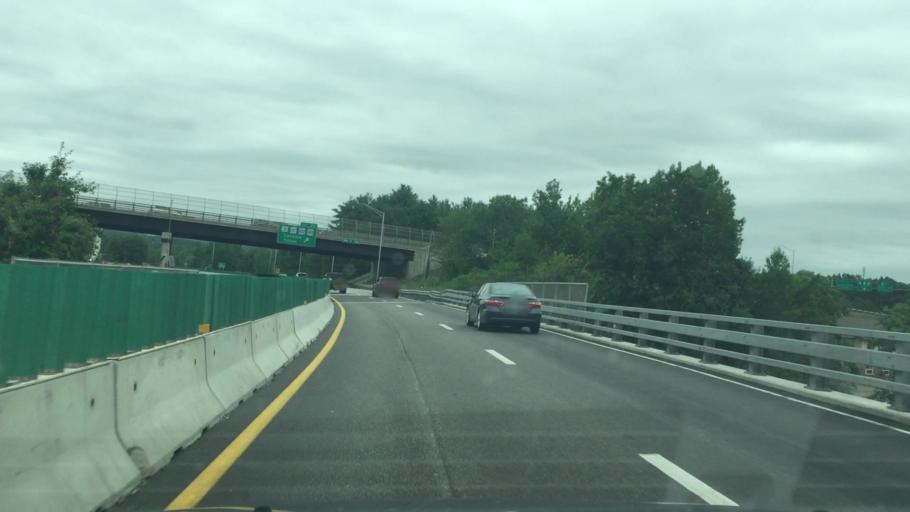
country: US
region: New Hampshire
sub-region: Belknap County
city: Tilton
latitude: 43.4520
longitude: -71.5701
